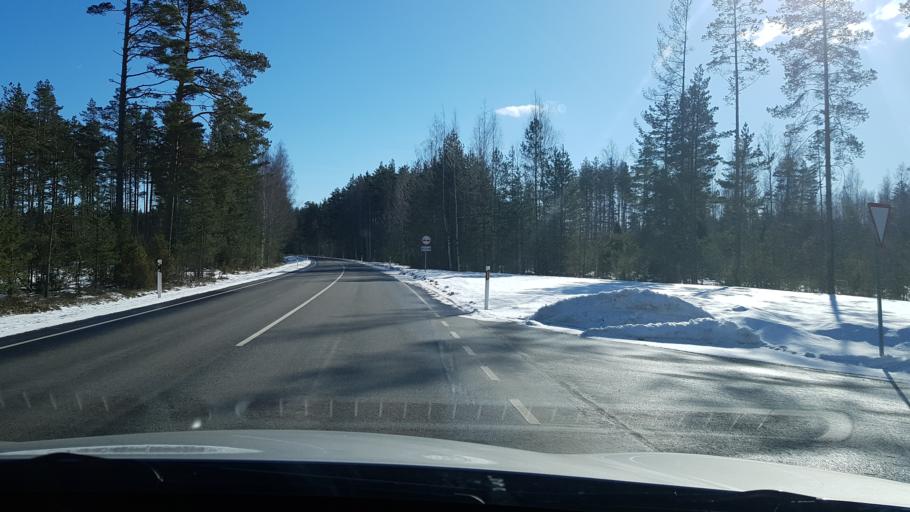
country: EE
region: Polvamaa
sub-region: Raepina vald
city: Rapina
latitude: 57.9828
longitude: 27.5668
